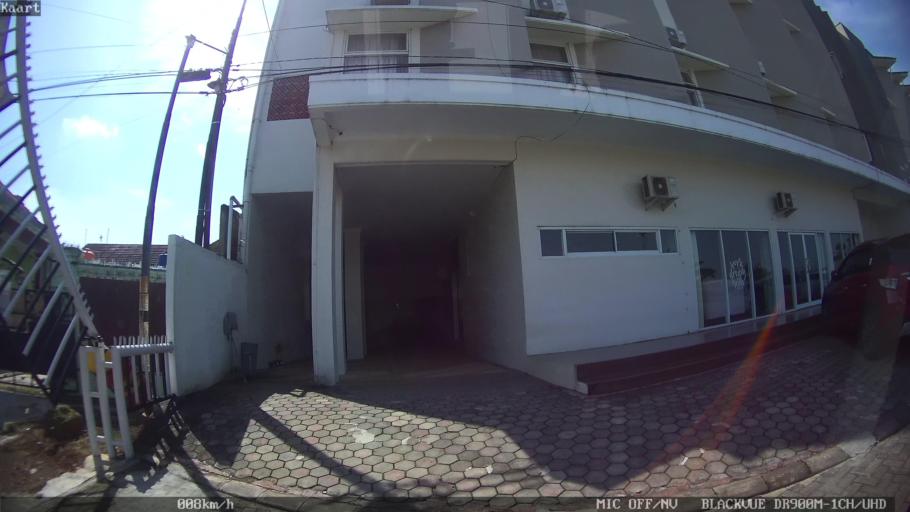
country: ID
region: Lampung
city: Kedaton
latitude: -5.3704
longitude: 105.2441
